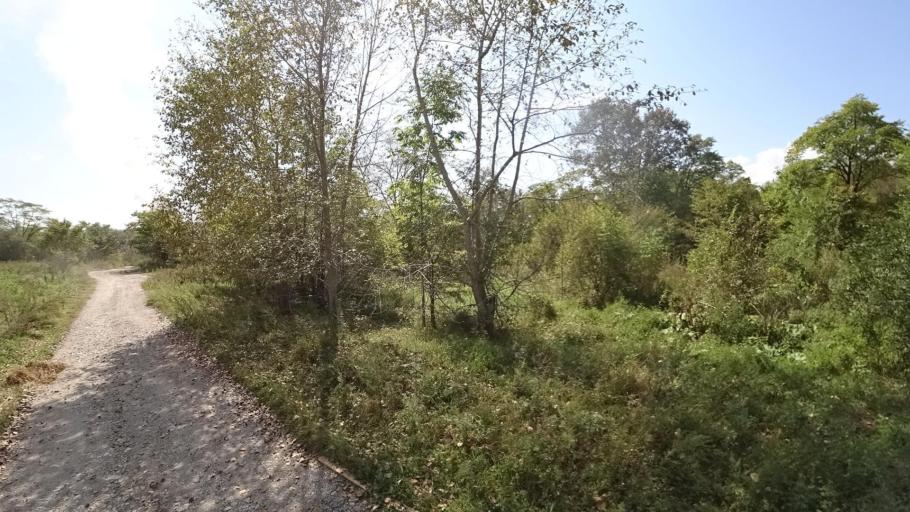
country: RU
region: Jewish Autonomous Oblast
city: Londoko
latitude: 49.0123
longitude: 131.8967
